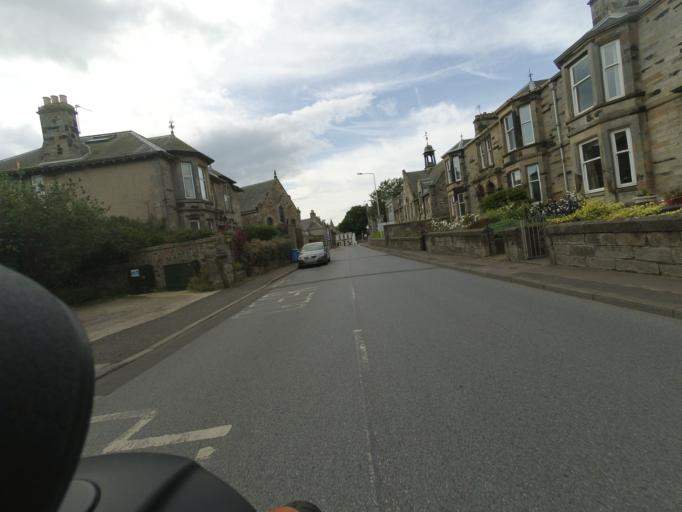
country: GB
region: Scotland
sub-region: Fife
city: Anstruther
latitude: 56.2240
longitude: -2.7018
